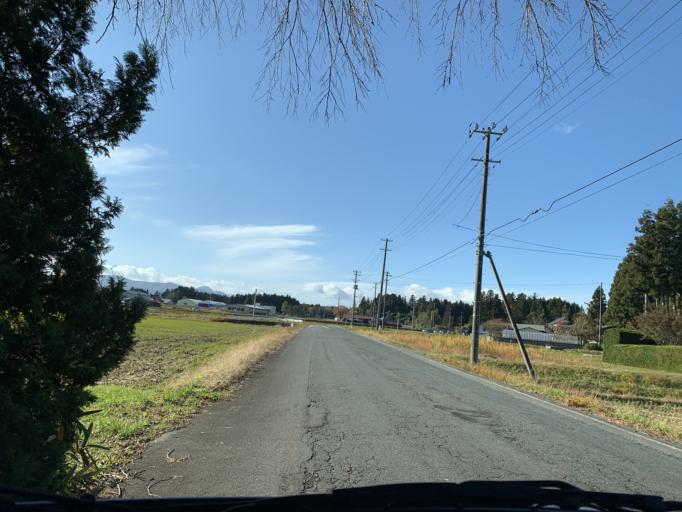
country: JP
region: Iwate
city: Mizusawa
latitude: 39.0858
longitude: 141.0946
